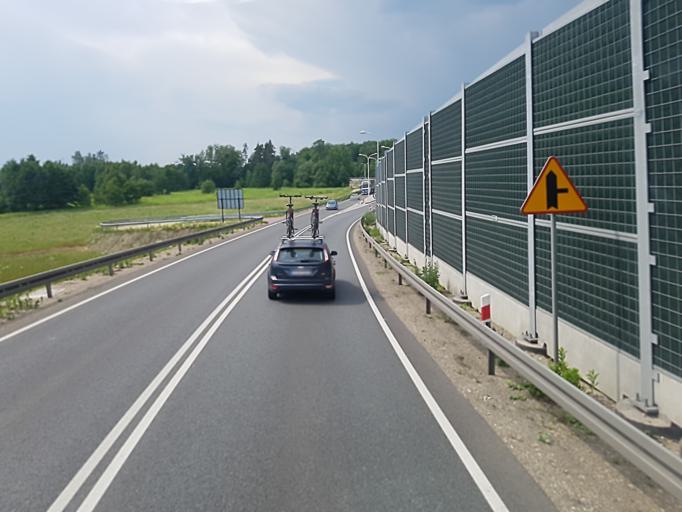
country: PL
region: Silesian Voivodeship
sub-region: Powiat pszczynski
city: Pawlowice
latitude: 49.9554
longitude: 18.6859
